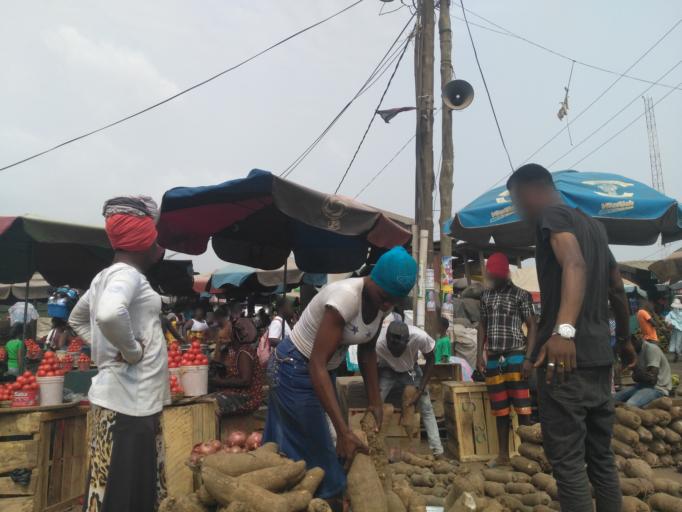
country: GH
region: Greater Accra
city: Accra
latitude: 5.5496
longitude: -0.2198
